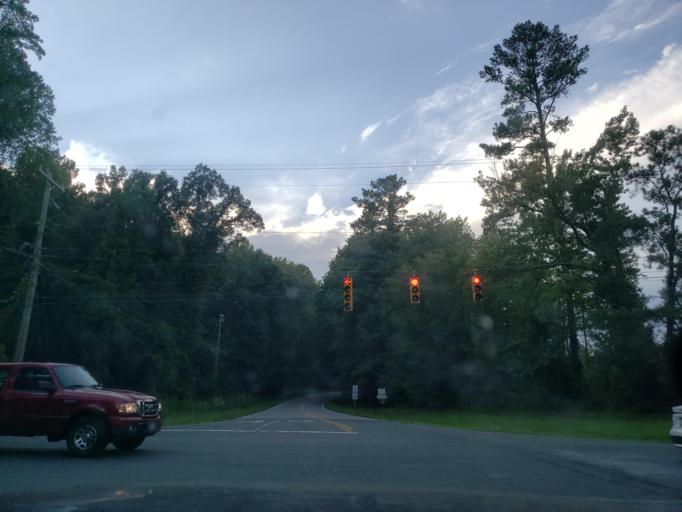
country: US
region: North Carolina
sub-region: Durham County
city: Durham
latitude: 35.9946
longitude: -78.9741
